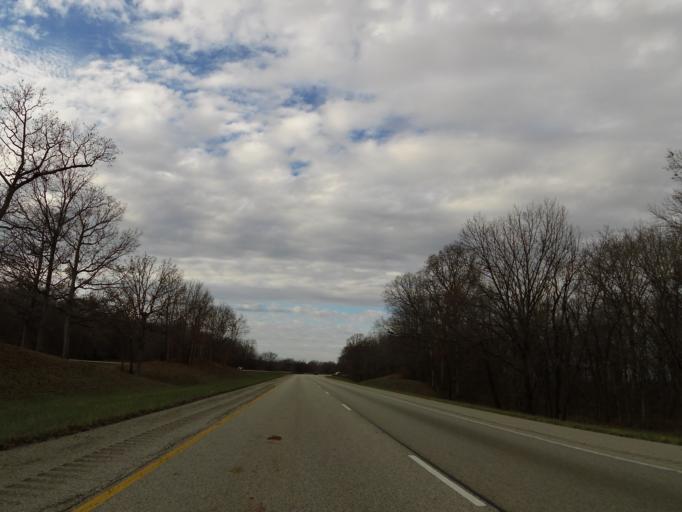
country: US
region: Illinois
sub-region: Washington County
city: Nashville
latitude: 38.3913
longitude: -89.3220
